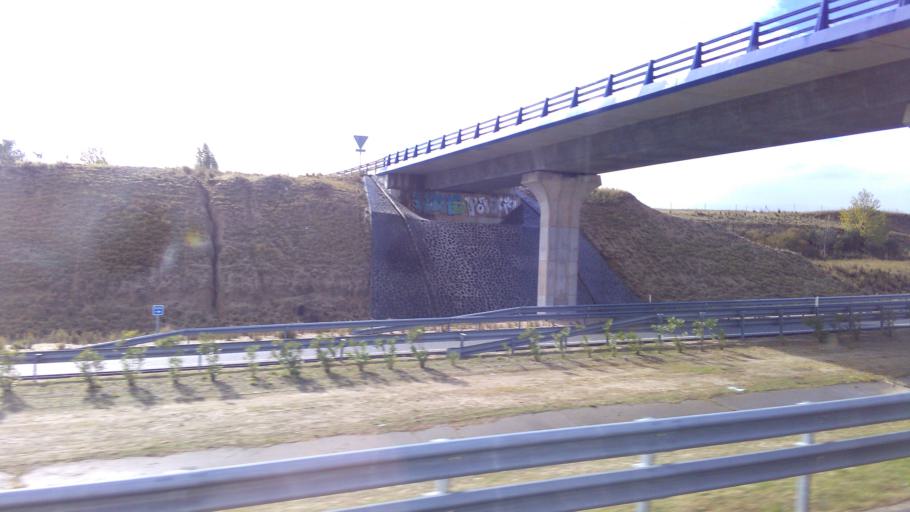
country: ES
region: Madrid
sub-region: Provincia de Madrid
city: Navalcarnero
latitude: 40.2670
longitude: -4.0076
